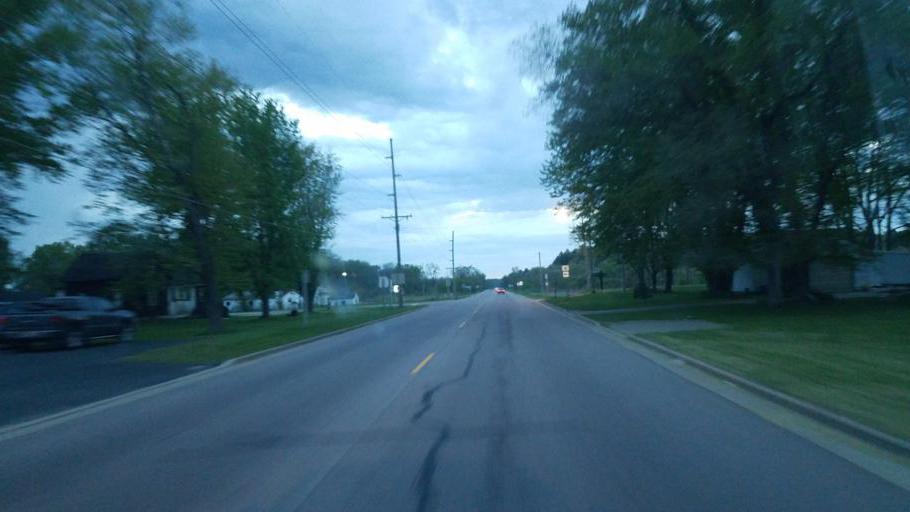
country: US
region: Wisconsin
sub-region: Juneau County
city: Elroy
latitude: 43.6869
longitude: -90.2662
